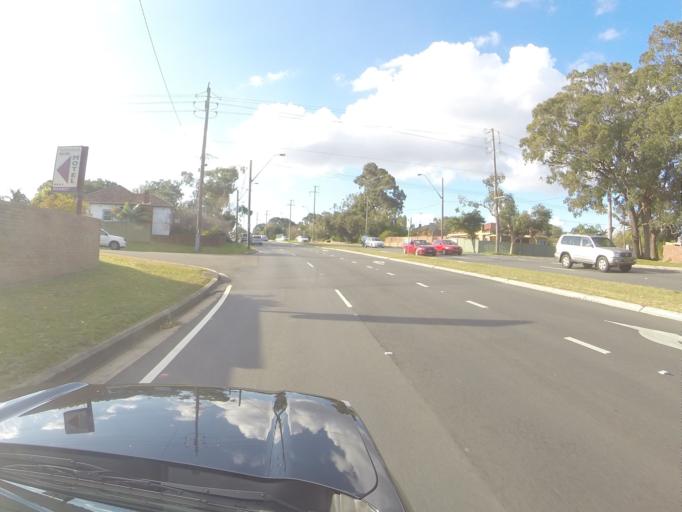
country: AU
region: New South Wales
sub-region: Sutherland Shire
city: Kirrawee
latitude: -34.0371
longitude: 151.0656
